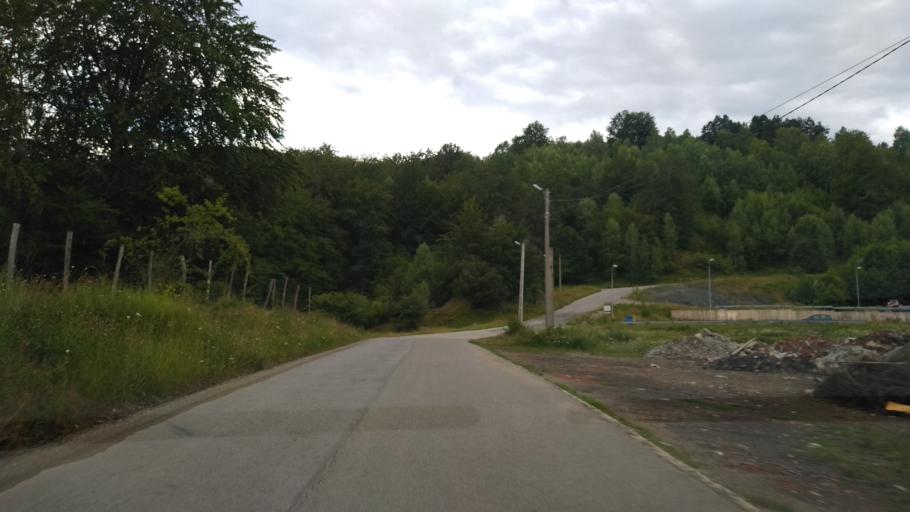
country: RO
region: Hunedoara
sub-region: Municipiul  Vulcan
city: Jiu-Paroseni
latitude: 45.3549
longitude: 23.2906
